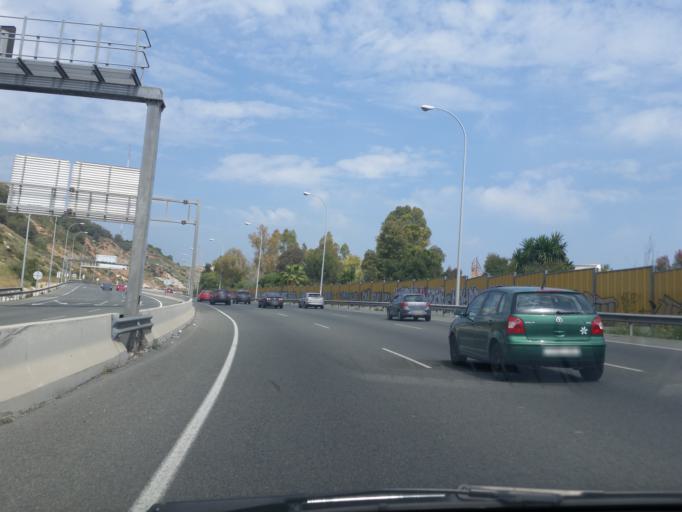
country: ES
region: Andalusia
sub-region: Provincia de Malaga
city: Malaga
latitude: 36.7269
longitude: -4.4536
